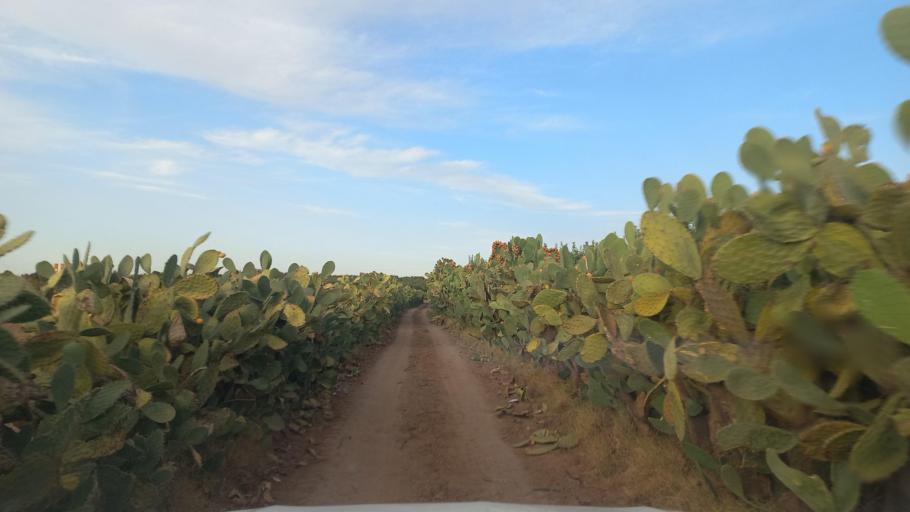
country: TN
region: Al Qasrayn
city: Kasserine
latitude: 35.2543
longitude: 9.0423
